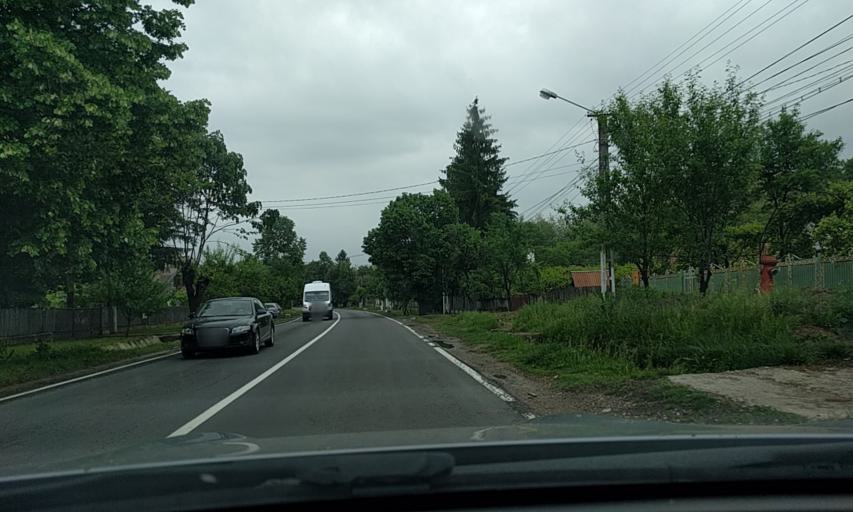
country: RO
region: Dambovita
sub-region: Comuna Branesti
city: Branesti
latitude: 45.0302
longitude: 25.4241
